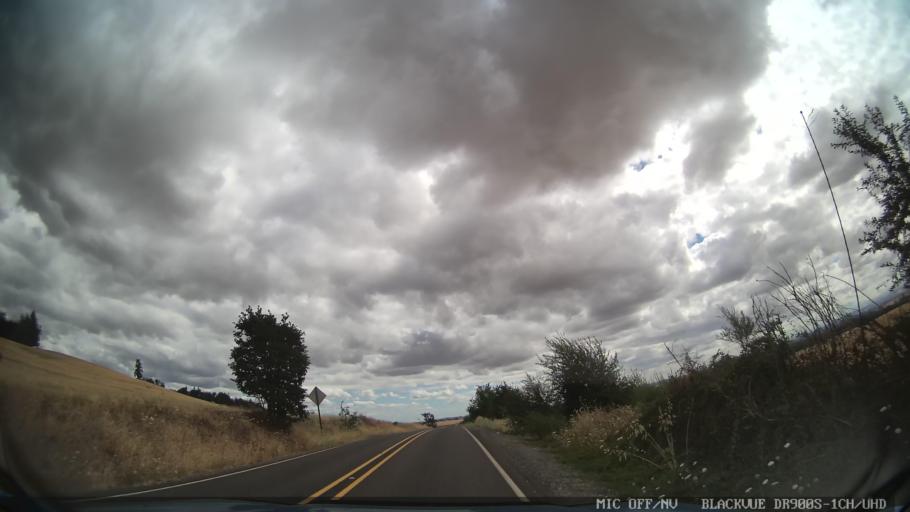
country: US
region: Oregon
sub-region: Marion County
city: Sublimity
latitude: 44.8673
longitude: -122.7395
